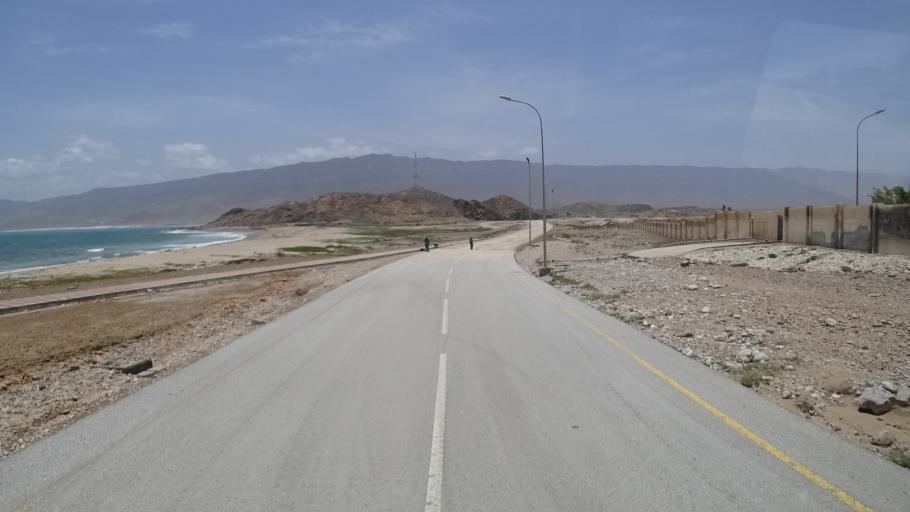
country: OM
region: Zufar
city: Salalah
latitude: 16.9930
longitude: 54.6916
